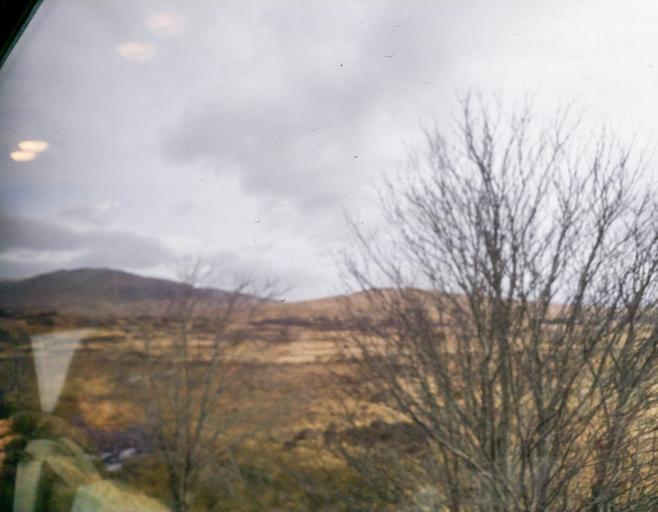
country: GB
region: Scotland
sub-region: Highland
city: Spean Bridge
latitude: 56.6875
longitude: -4.5765
